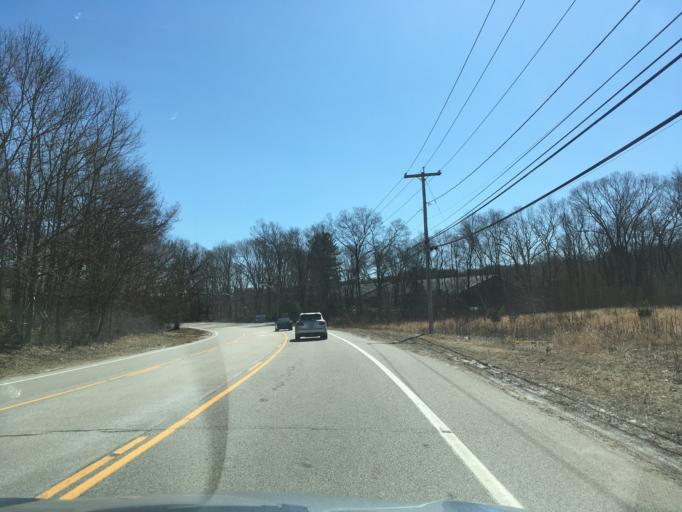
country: US
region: Rhode Island
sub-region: Washington County
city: Exeter
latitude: 41.5882
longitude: -71.5019
